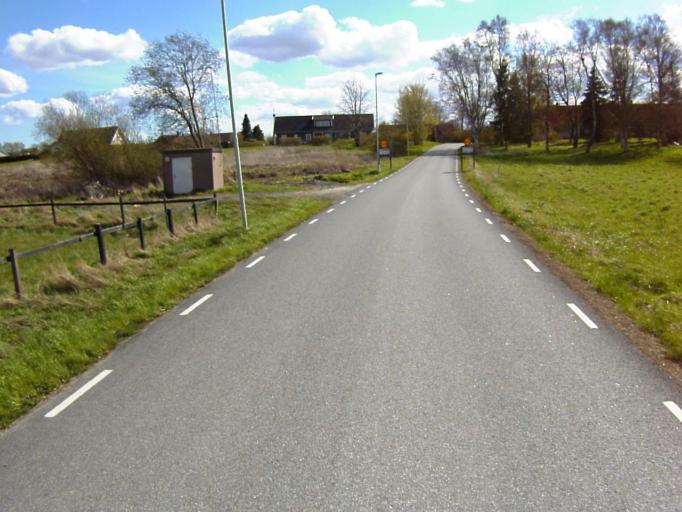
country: SE
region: Skane
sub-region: Kristianstads Kommun
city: Kristianstad
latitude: 56.0127
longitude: 14.0909
